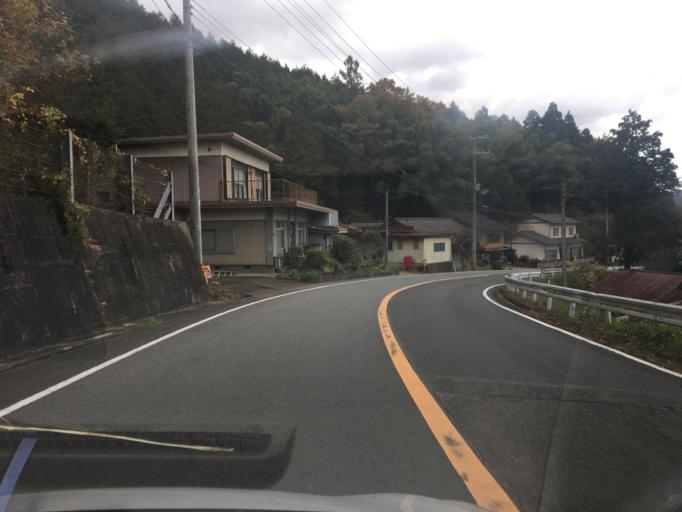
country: JP
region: Hyogo
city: Toyooka
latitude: 35.4637
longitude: 134.7361
